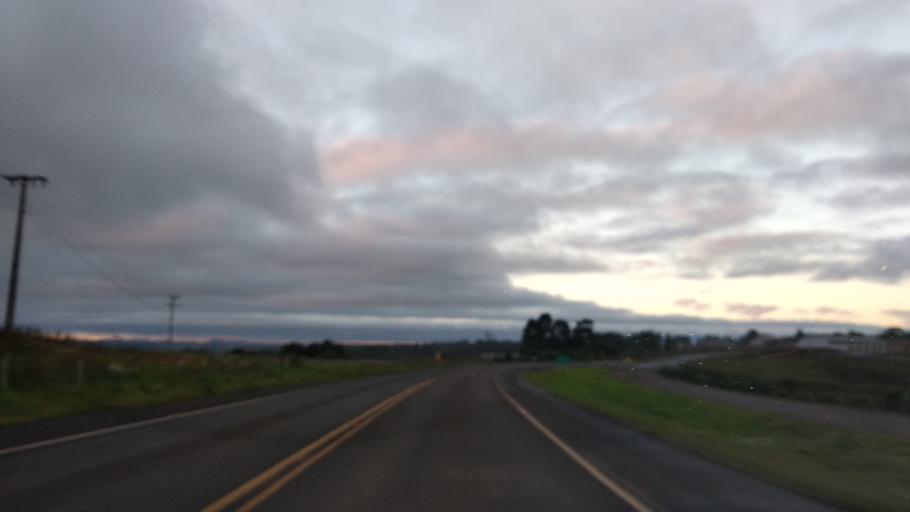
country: BR
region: Santa Catarina
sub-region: Campos Novos
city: Campos Novos
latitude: -27.3720
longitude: -51.2031
